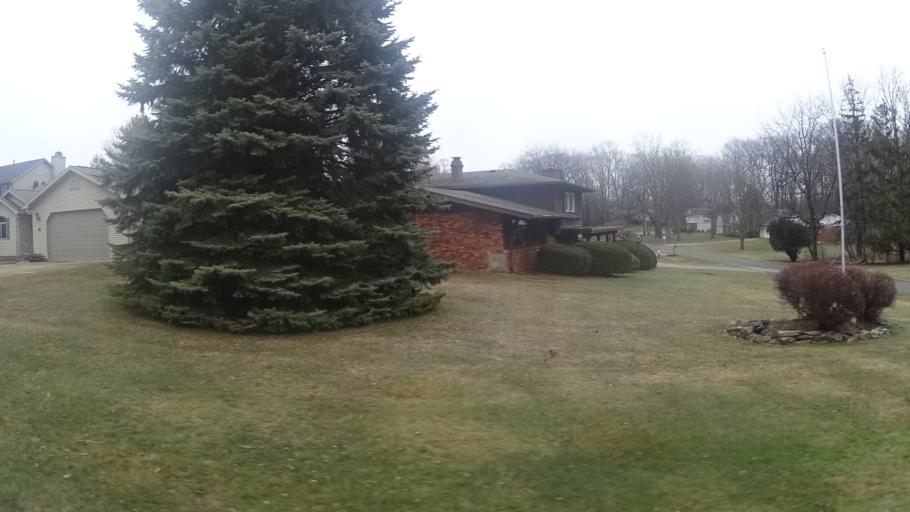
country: US
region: Ohio
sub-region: Erie County
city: Sandusky
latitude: 41.4179
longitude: -82.6471
